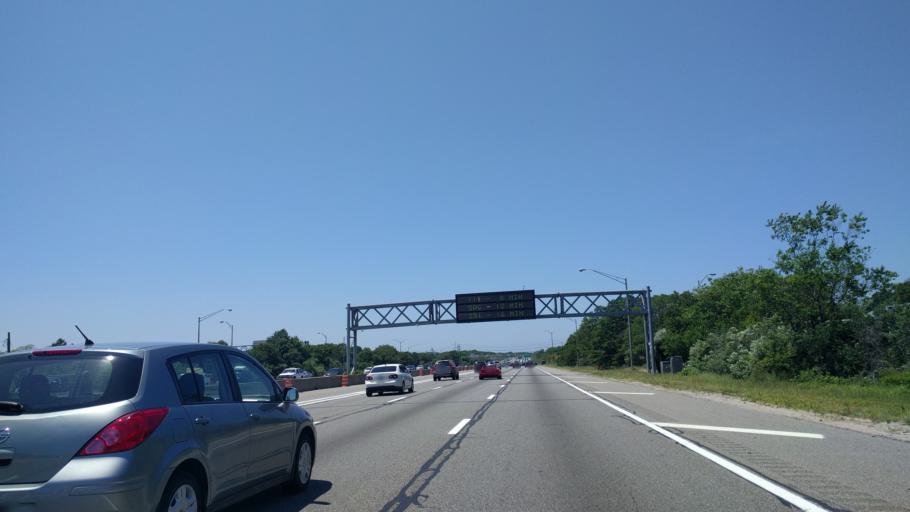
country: US
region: New York
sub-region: Suffolk County
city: Holtsville
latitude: 40.8196
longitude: -73.0582
